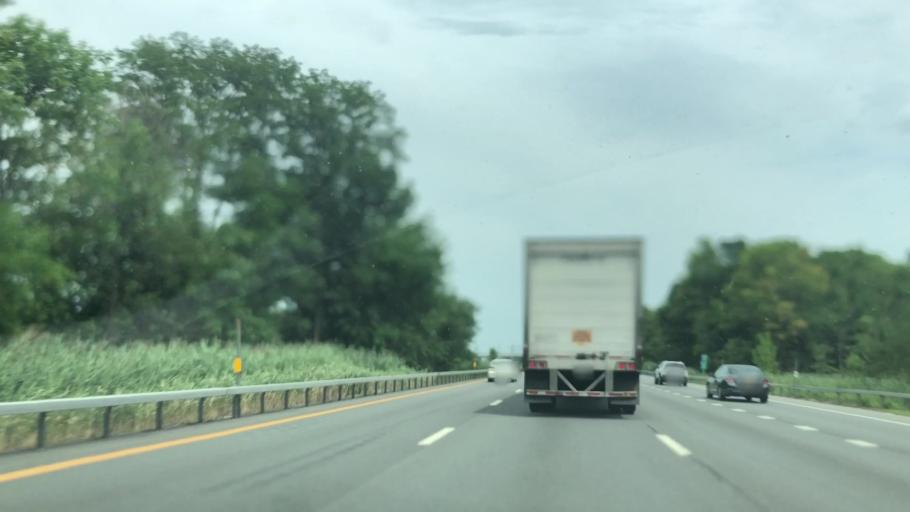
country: US
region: New York
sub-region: Albany County
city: Roessleville
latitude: 42.7473
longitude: -73.7739
